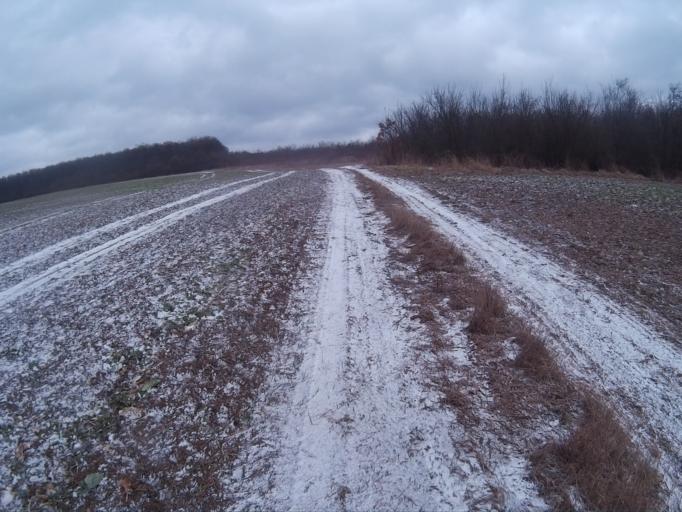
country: HU
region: Borsod-Abauj-Zemplen
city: Halmaj
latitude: 48.3722
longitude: 20.9563
